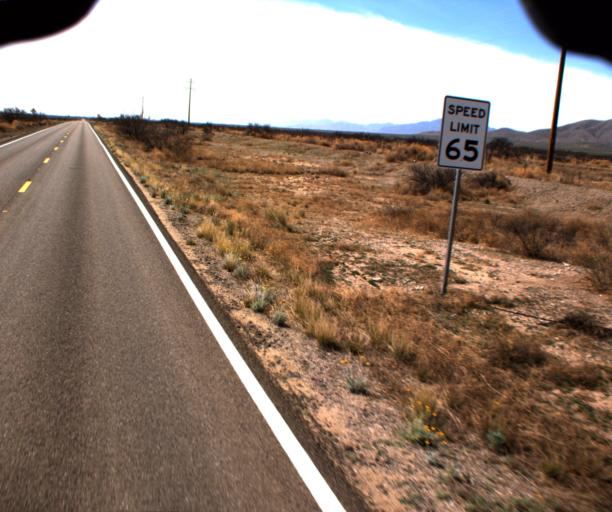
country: US
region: Arizona
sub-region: Cochise County
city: Willcox
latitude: 32.1704
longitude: -109.9465
